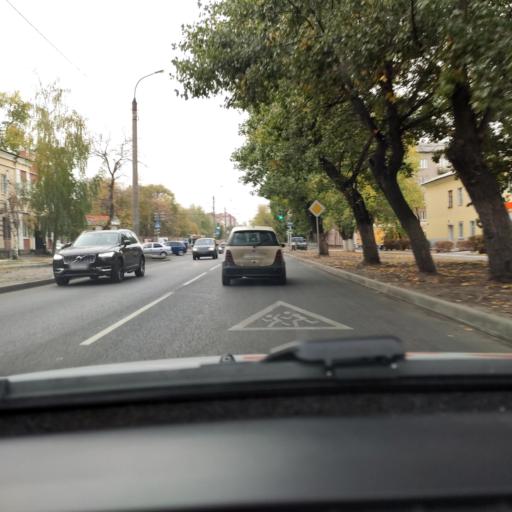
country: RU
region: Voronezj
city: Voronezh
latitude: 51.6434
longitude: 39.2415
